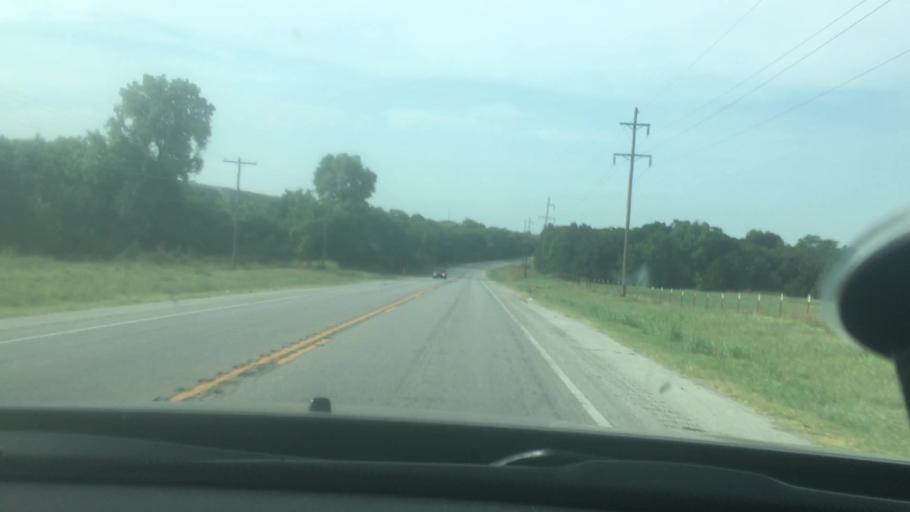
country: US
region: Oklahoma
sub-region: Carter County
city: Ardmore
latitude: 34.1264
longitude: -97.1430
